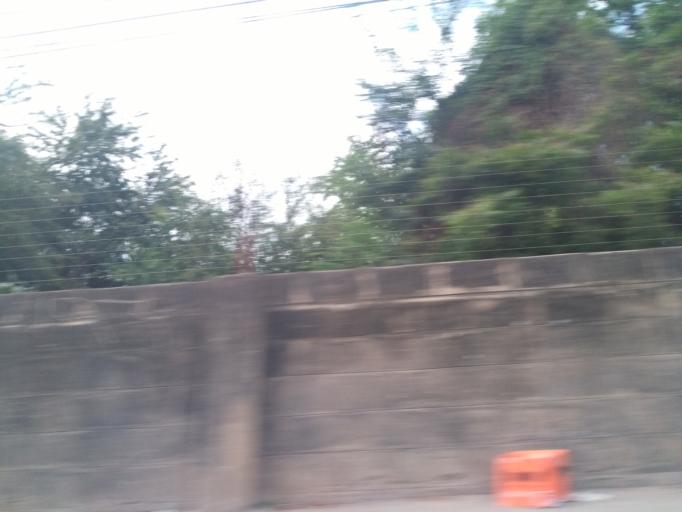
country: TZ
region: Dar es Salaam
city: Magomeni
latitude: -6.7686
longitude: 39.2701
